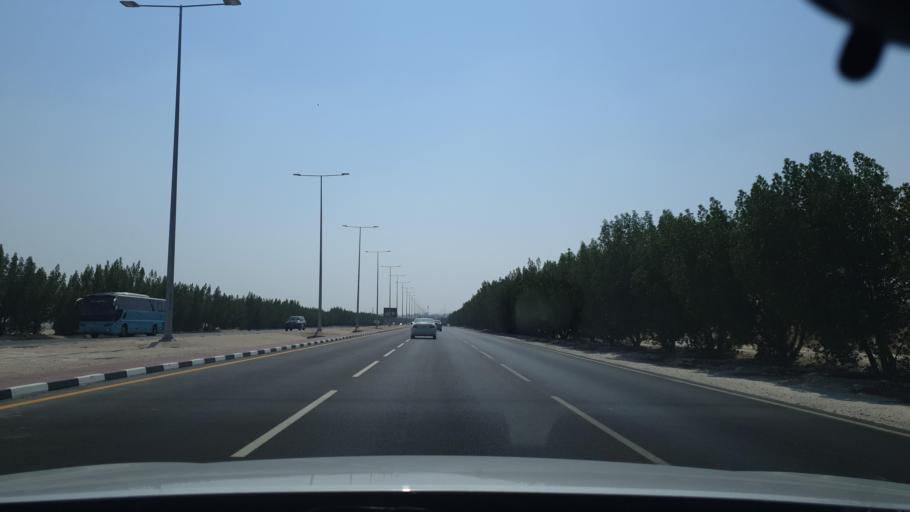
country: QA
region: Al Khawr
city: Al Khawr
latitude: 25.7031
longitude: 51.5036
